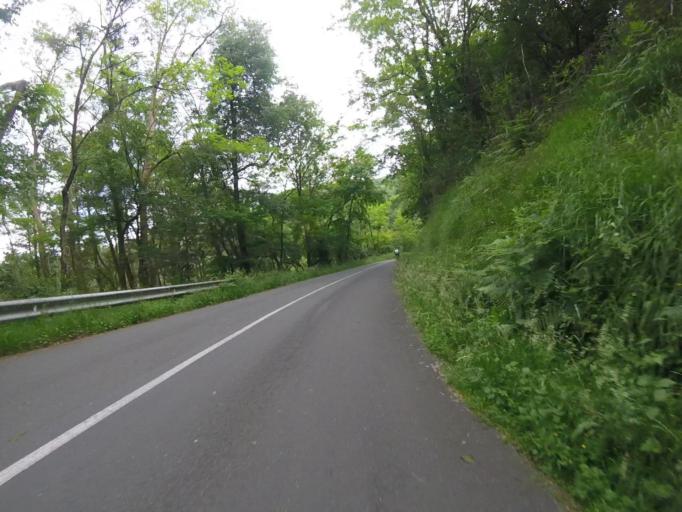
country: ES
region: Basque Country
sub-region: Provincia de Guipuzcoa
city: Errenteria
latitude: 43.2772
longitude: -1.8527
